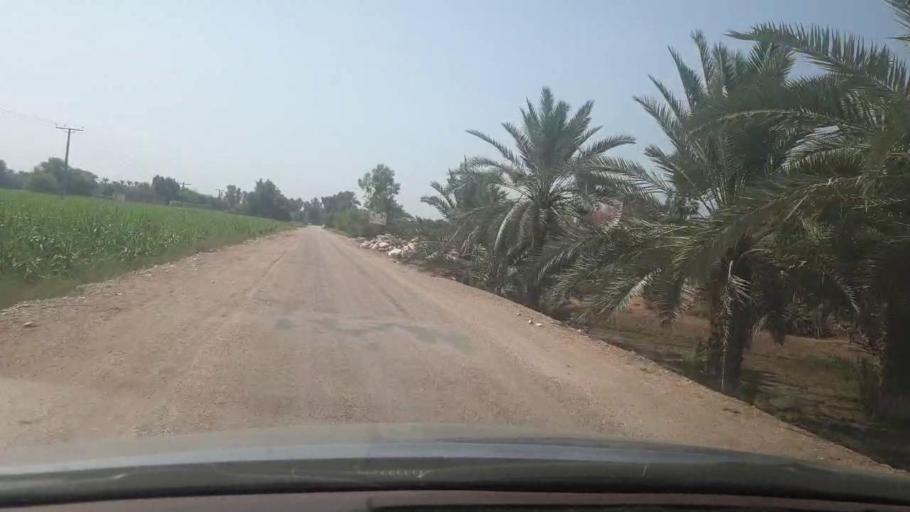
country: PK
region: Sindh
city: Ranipur
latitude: 27.2848
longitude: 68.5796
